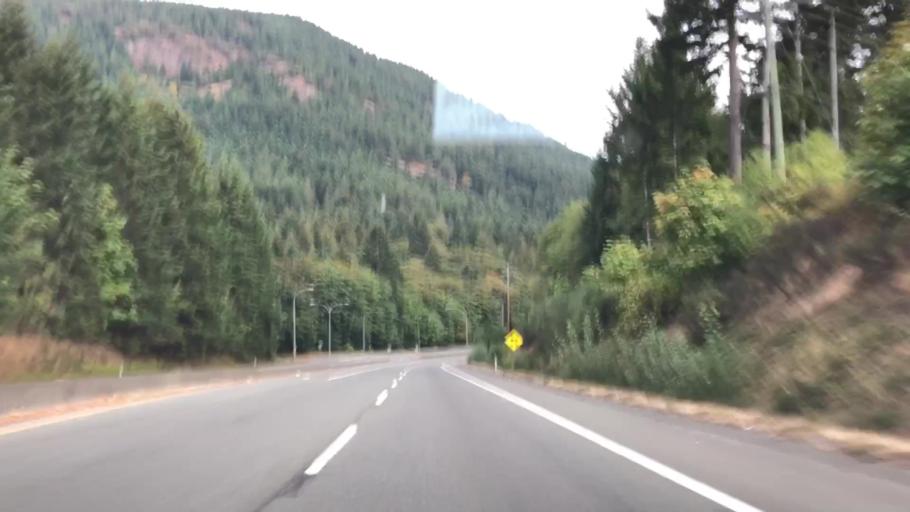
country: CA
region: British Columbia
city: North Cowichan
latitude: 48.8477
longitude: -123.7212
